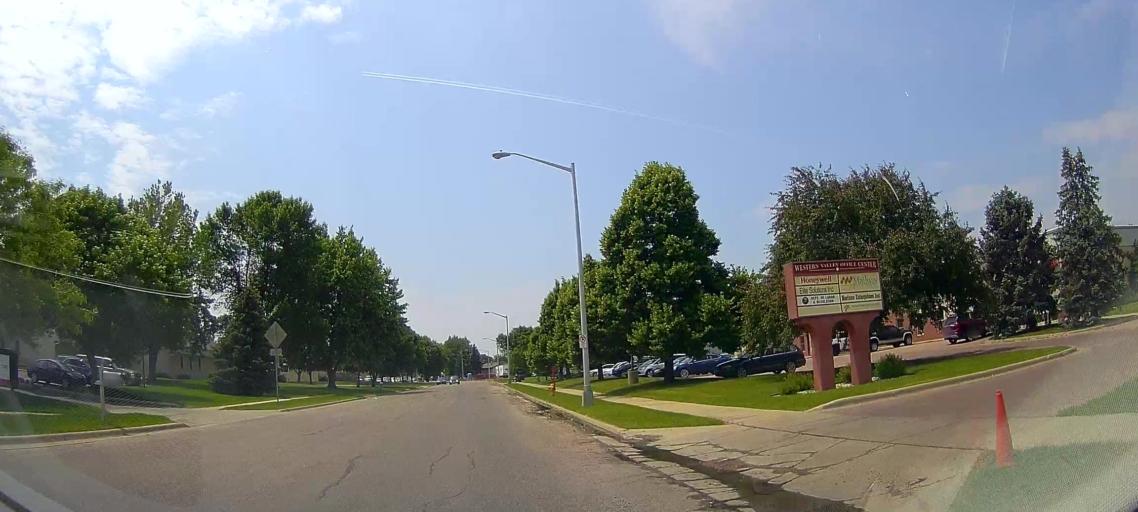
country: US
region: South Dakota
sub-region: Minnehaha County
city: Sioux Falls
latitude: 43.5077
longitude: -96.7423
